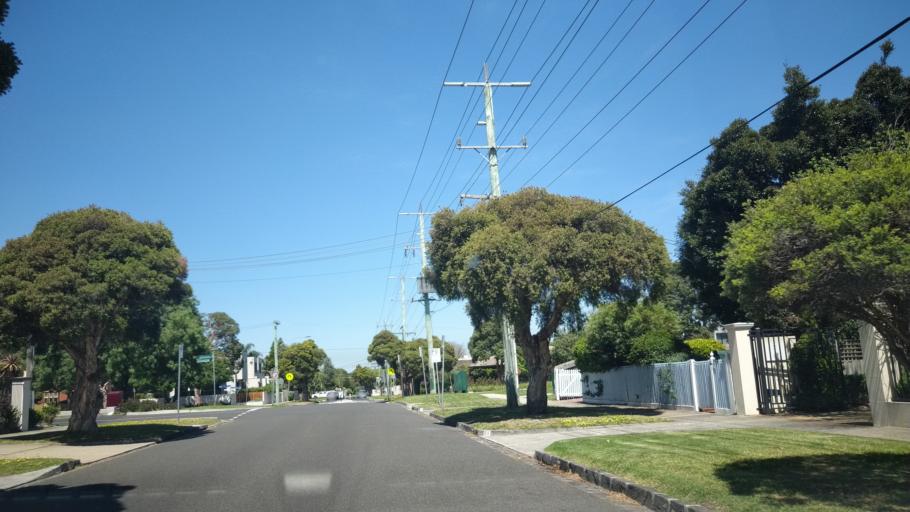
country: AU
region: Victoria
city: Ormond
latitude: -37.8958
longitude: 145.0318
